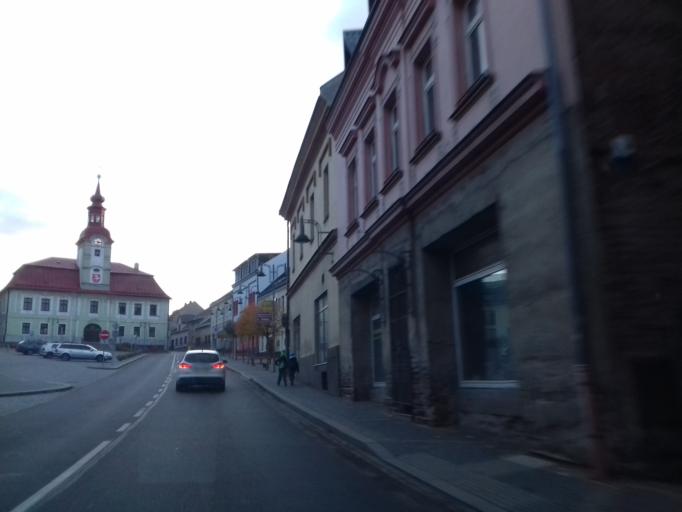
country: CZ
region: Pardubicky
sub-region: Okres Chrudim
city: Hlinsko
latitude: 49.7609
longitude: 15.9064
